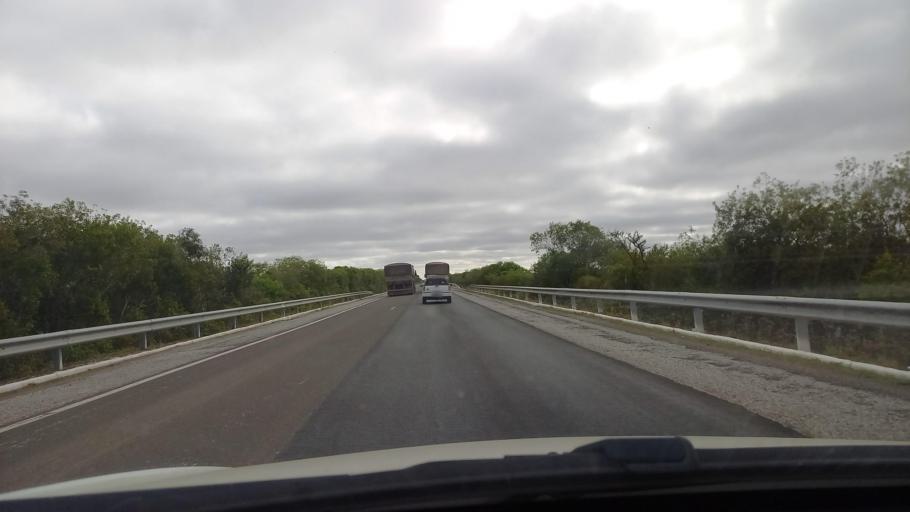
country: BR
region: Rio Grande do Sul
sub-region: Dom Pedrito
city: Dom Pedrito
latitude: -30.9465
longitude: -54.7164
